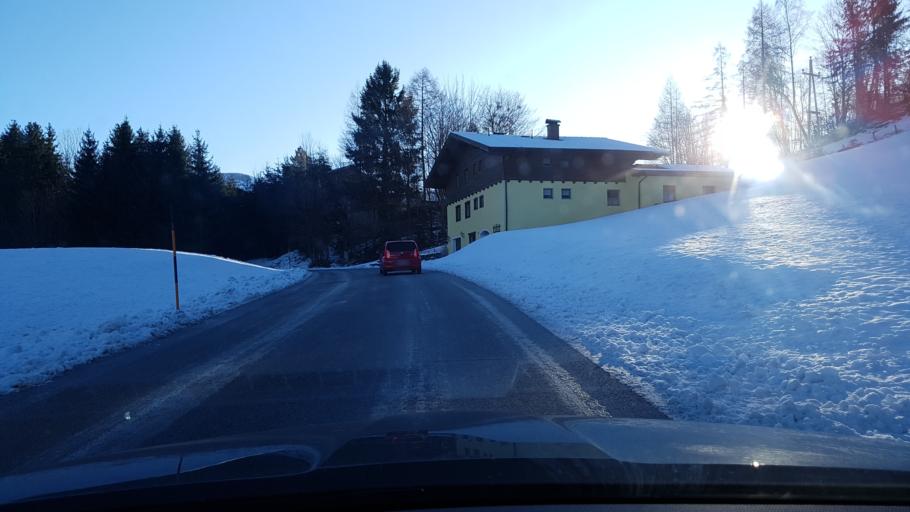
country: AT
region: Salzburg
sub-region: Politischer Bezirk Hallein
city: Kuchl
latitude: 47.6539
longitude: 13.1989
